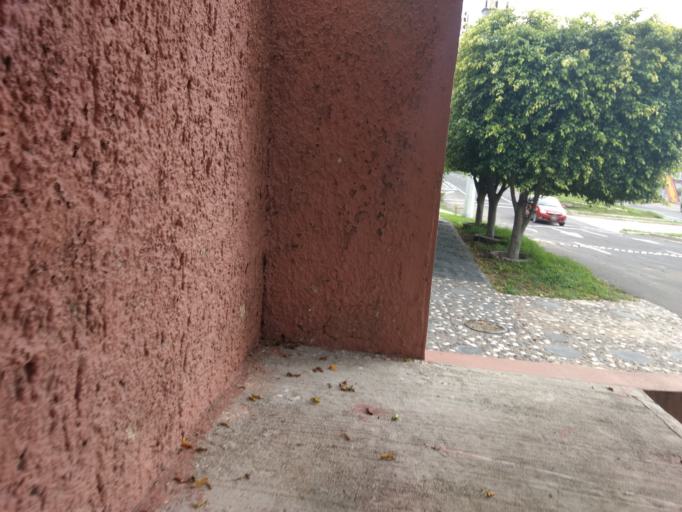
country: MX
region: Jalisco
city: Guadalajara
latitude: 20.6677
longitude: -103.4363
